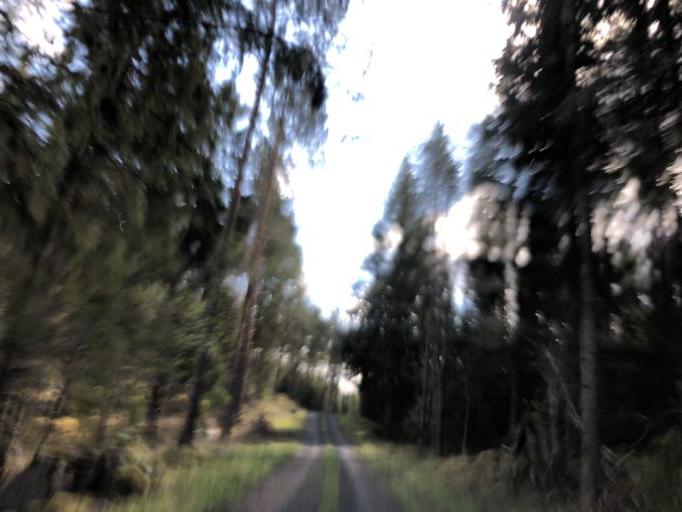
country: SE
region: Uppsala
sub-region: Heby Kommun
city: Tarnsjo
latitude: 60.2316
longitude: 16.7202
